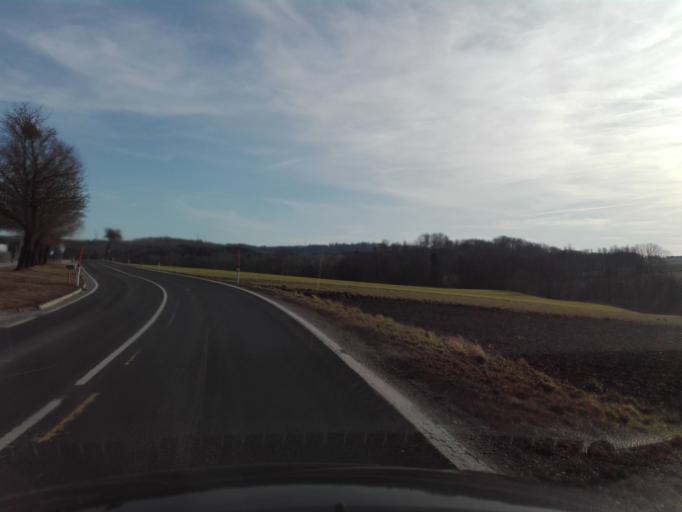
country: AT
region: Lower Austria
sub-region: Politischer Bezirk Amstetten
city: Amstetten
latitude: 48.1679
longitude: 14.8390
